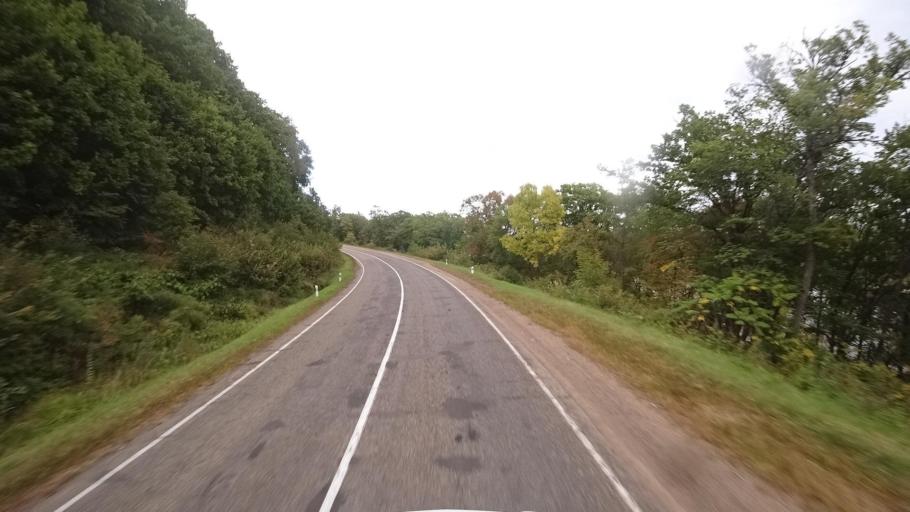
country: RU
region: Primorskiy
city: Yakovlevka
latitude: 44.3919
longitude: 133.4692
